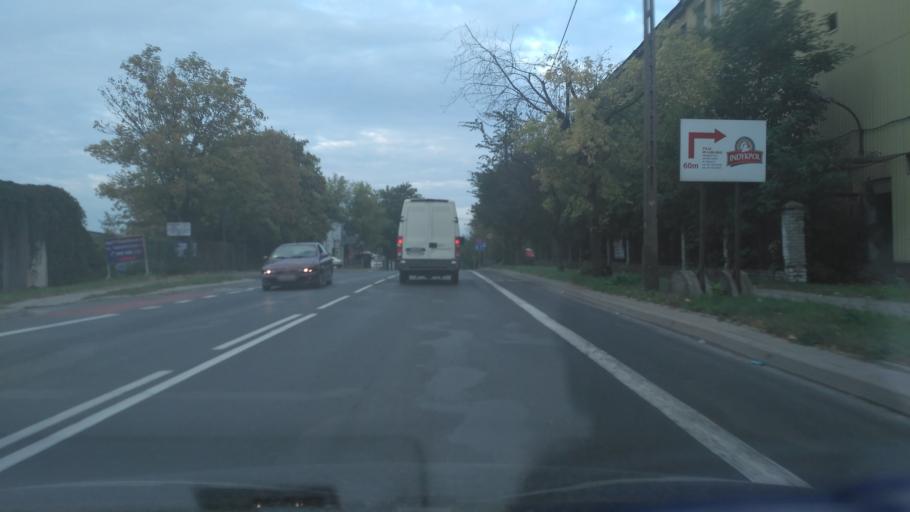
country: PL
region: Lublin Voivodeship
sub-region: Powiat lubelski
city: Jakubowice Murowane
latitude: 51.2549
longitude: 22.6049
